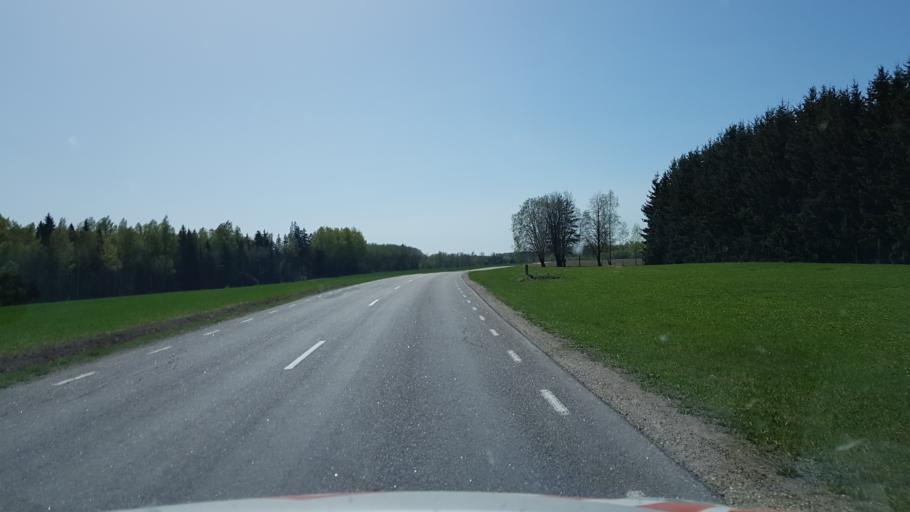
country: EE
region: Viljandimaa
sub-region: Suure-Jaani vald
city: Suure-Jaani
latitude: 58.5084
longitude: 25.4608
